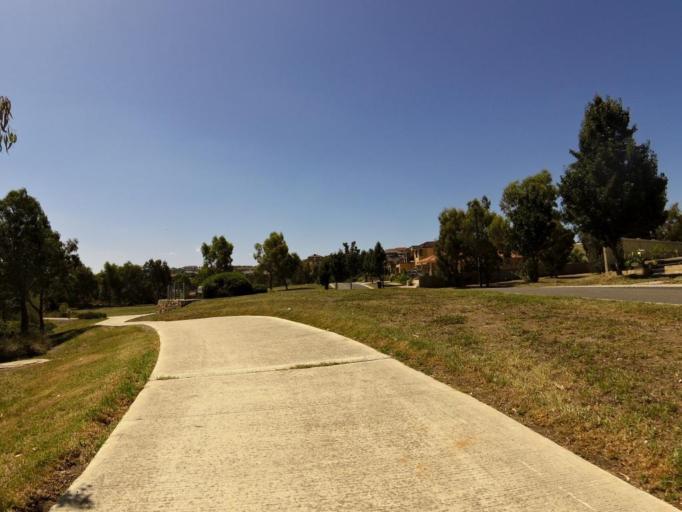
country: AU
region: Victoria
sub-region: Hume
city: Meadow Heights
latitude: -37.6485
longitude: 144.9071
